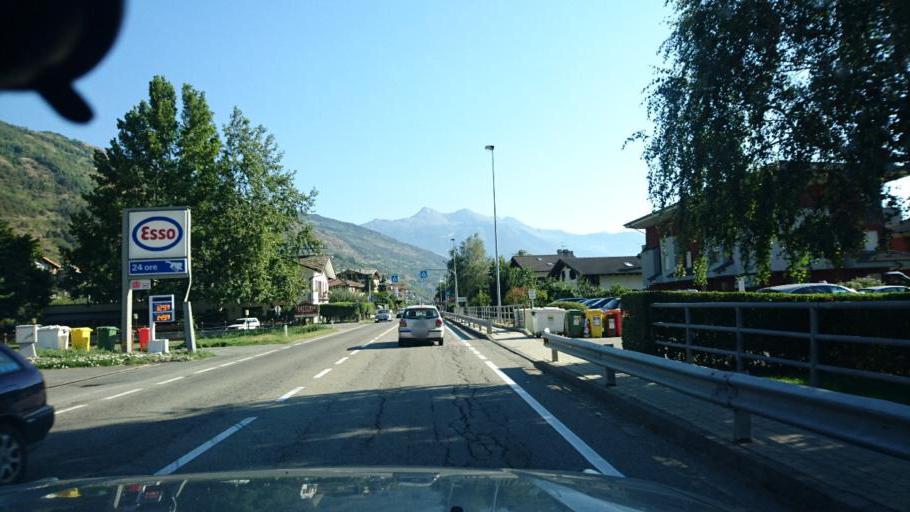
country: IT
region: Aosta Valley
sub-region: Valle d'Aosta
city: Saint Maurice
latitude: 45.7154
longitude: 7.2589
